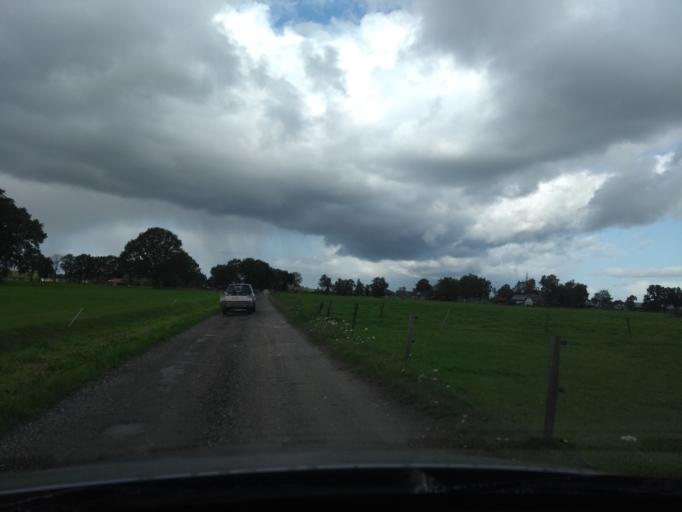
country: NL
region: Overijssel
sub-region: Gemeente Raalte
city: Raalte
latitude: 52.3652
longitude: 6.3390
